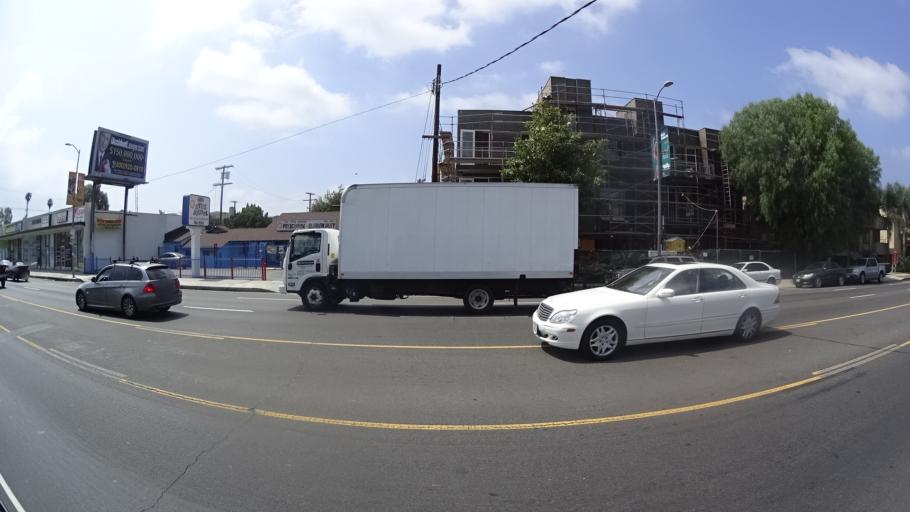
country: US
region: California
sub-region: Los Angeles County
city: Van Nuys
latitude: 34.1722
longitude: -118.4586
